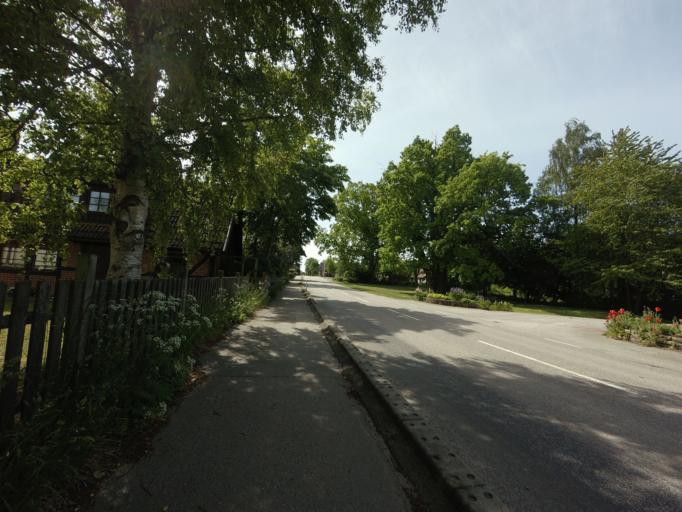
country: SE
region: Skane
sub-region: Helsingborg
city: Odakra
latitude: 56.1302
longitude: 12.6930
